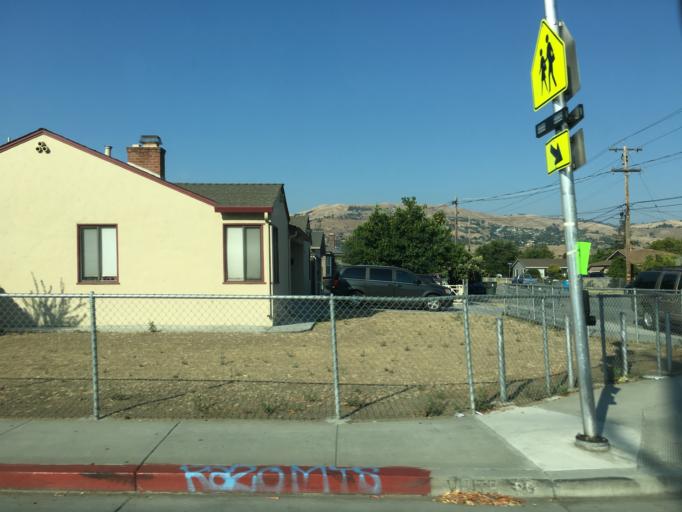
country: US
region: California
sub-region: Santa Clara County
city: Alum Rock
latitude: 37.3699
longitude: -121.8315
